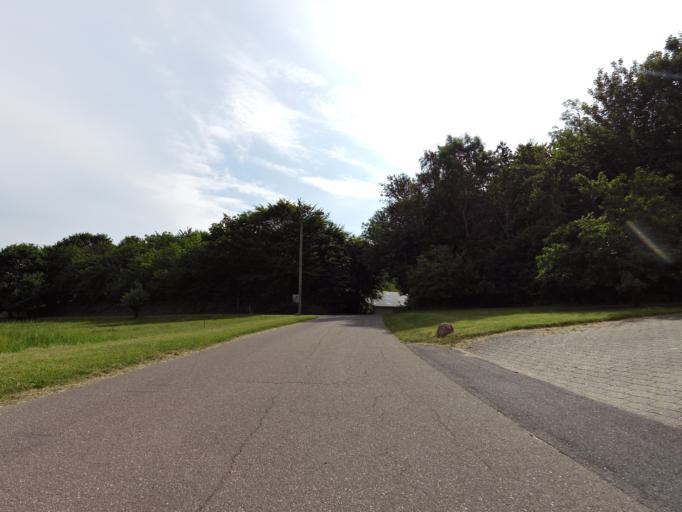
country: DK
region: Central Jutland
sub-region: Arhus Kommune
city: Kolt
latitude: 56.1274
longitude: 10.0574
